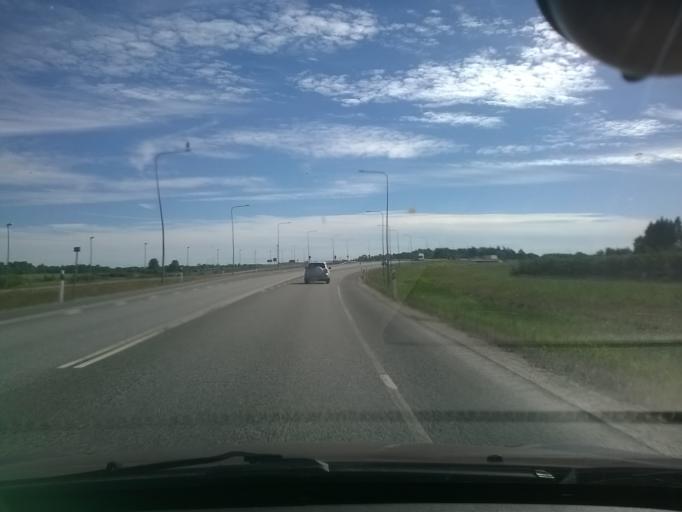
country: EE
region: Jaervamaa
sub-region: Paide linn
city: Paide
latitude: 58.9215
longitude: 25.6243
